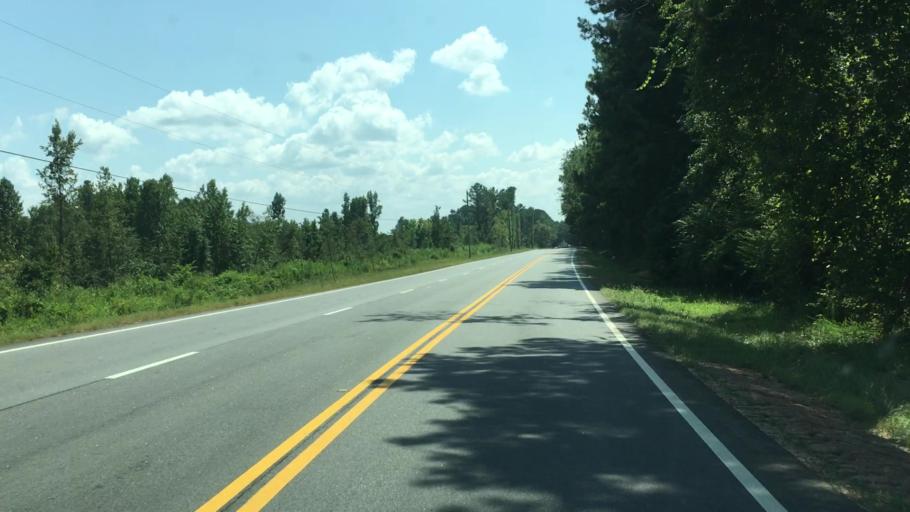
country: US
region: Georgia
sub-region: Oconee County
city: Watkinsville
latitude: 33.7373
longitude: -83.4289
